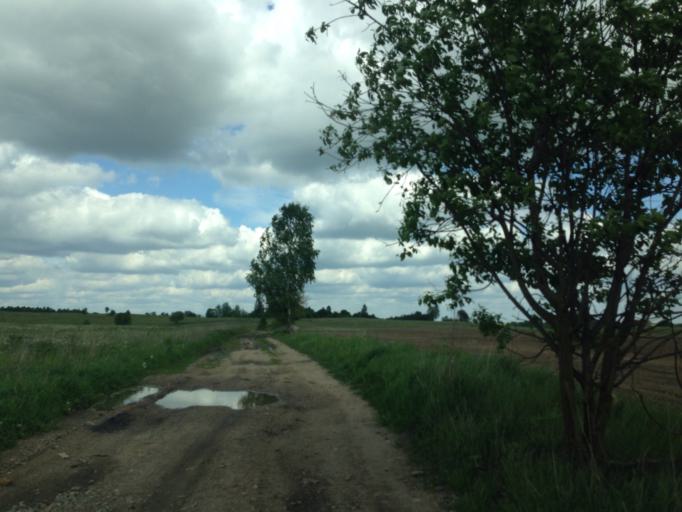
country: PL
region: Warmian-Masurian Voivodeship
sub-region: Powiat nidzicki
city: Kozlowo
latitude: 53.4309
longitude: 20.2785
